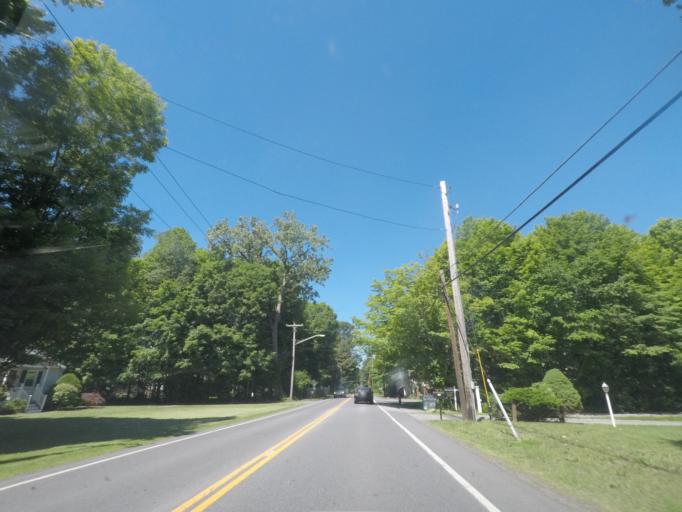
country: US
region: New York
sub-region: Saratoga County
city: Country Knolls
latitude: 42.8561
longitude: -73.7991
